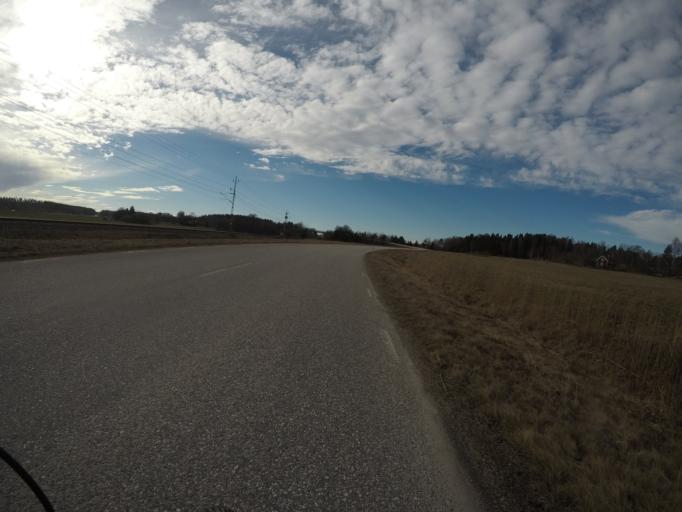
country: SE
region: Vaestmanland
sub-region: Kungsors Kommun
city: Kungsoer
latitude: 59.4205
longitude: 16.1709
